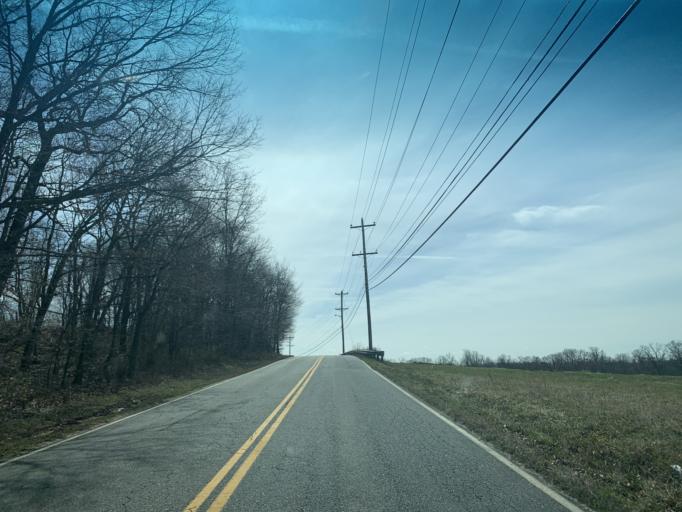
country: US
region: Maryland
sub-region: Cecil County
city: Perryville
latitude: 39.5764
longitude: -76.0253
